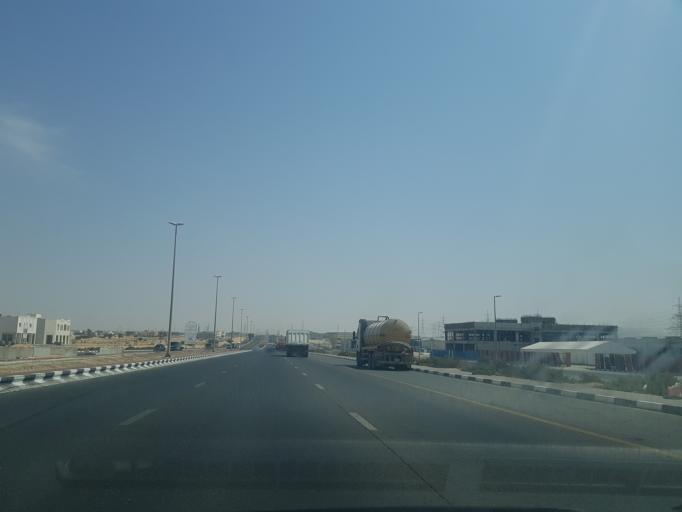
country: AE
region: Ash Shariqah
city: Sharjah
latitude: 25.2494
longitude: 55.5368
